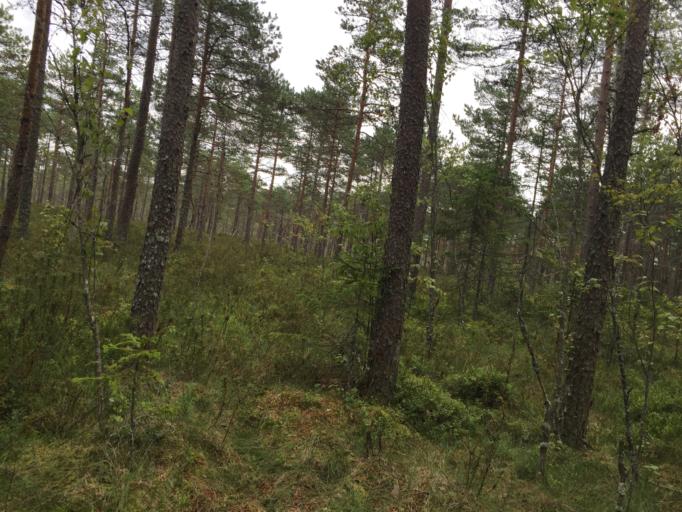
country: LV
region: Pargaujas
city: Stalbe
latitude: 57.3139
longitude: 25.0480
